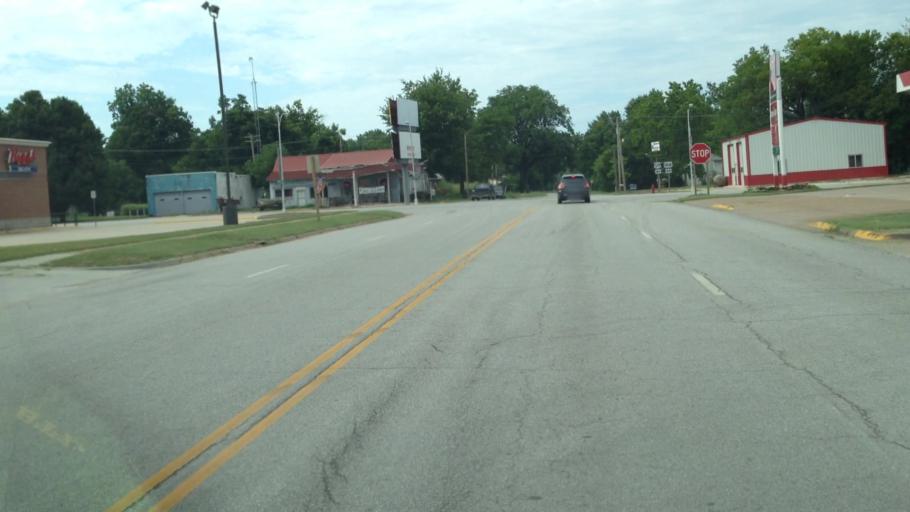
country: US
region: Kansas
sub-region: Labette County
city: Chetopa
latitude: 37.0362
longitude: -95.0861
